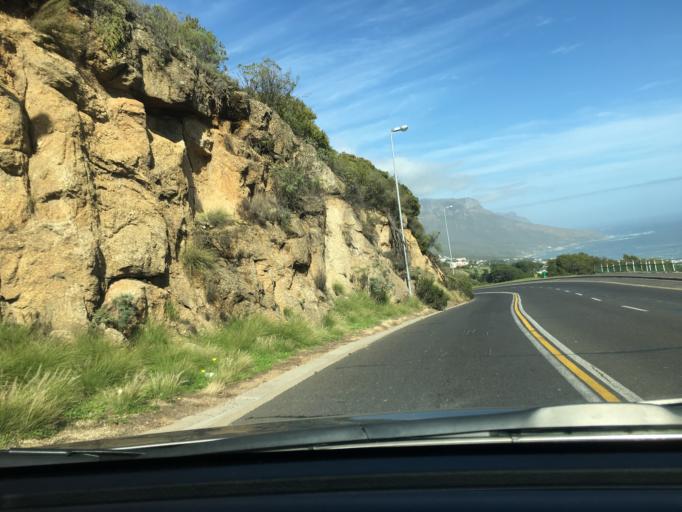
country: ZA
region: Western Cape
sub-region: City of Cape Town
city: Cape Town
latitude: -33.9443
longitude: 18.3930
